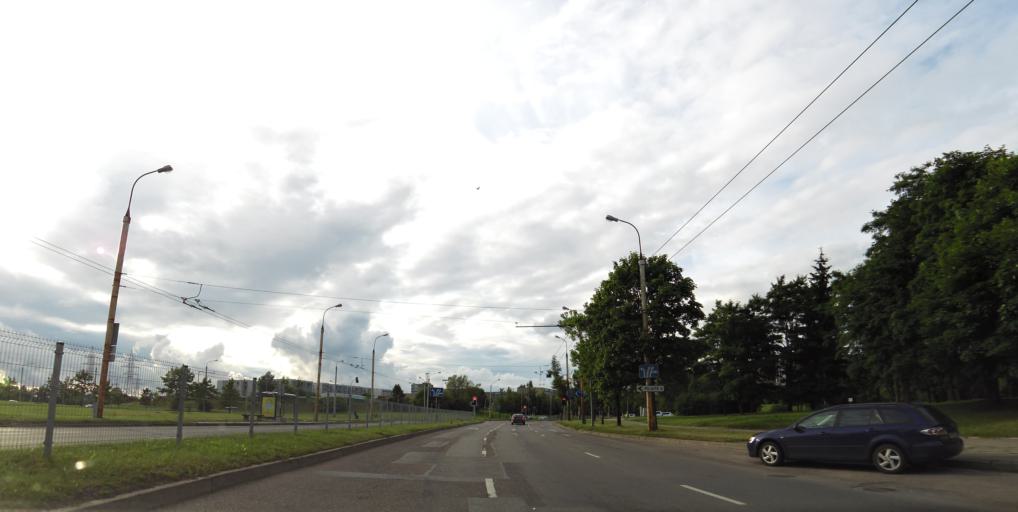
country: LT
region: Vilnius County
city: Justiniskes
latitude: 54.7051
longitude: 25.2163
